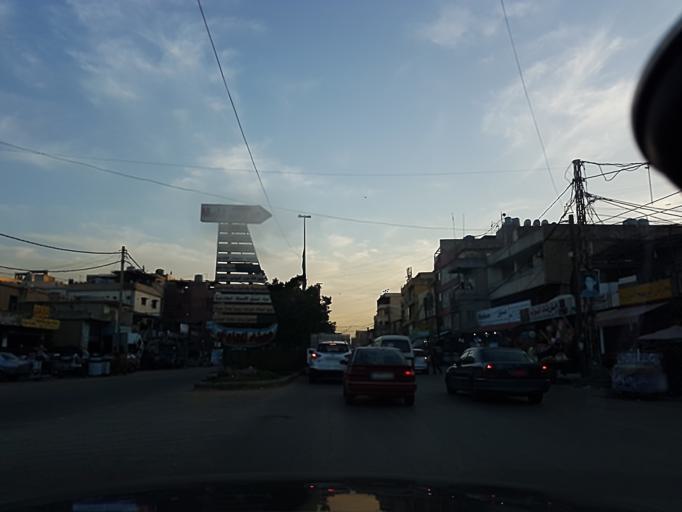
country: LB
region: Beyrouth
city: Beirut
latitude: 33.8370
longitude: 35.4846
